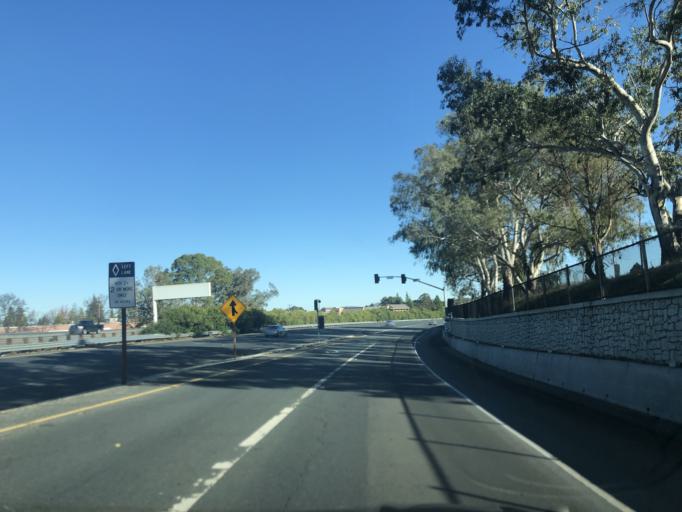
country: US
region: California
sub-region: Contra Costa County
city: Mountain View
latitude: 37.9957
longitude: -122.1181
